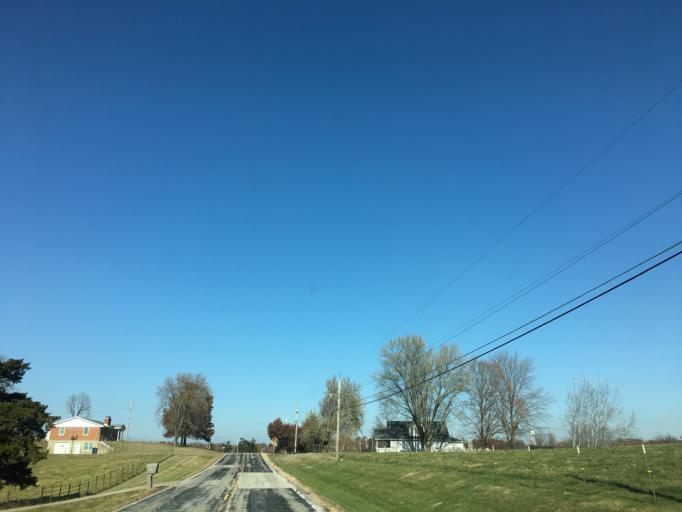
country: US
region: Missouri
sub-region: Cole County
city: Wardsville
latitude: 38.4727
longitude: -92.1777
